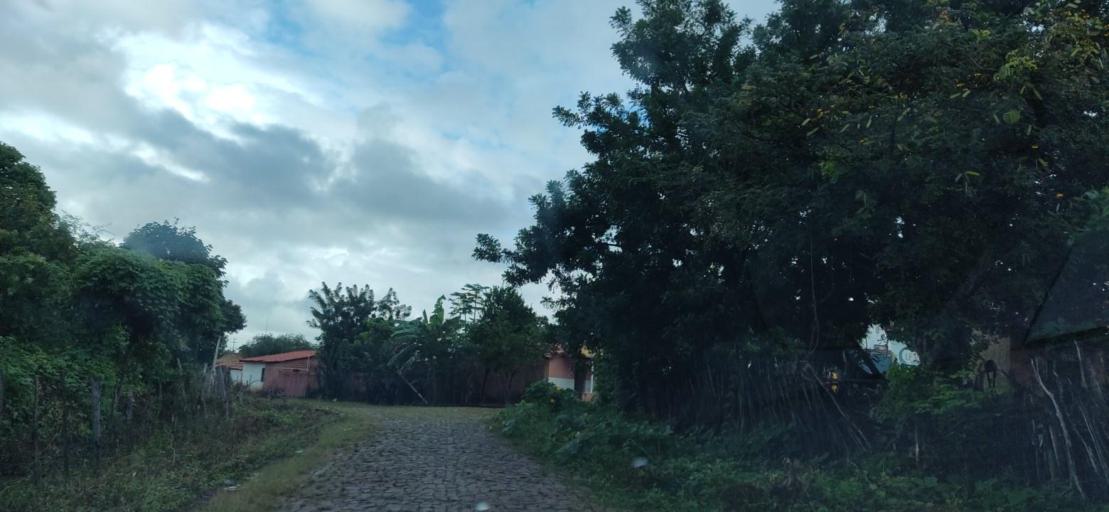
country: BR
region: Piaui
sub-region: Valenca Do Piaui
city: Valenca do Piaui
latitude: -6.1131
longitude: -41.7859
